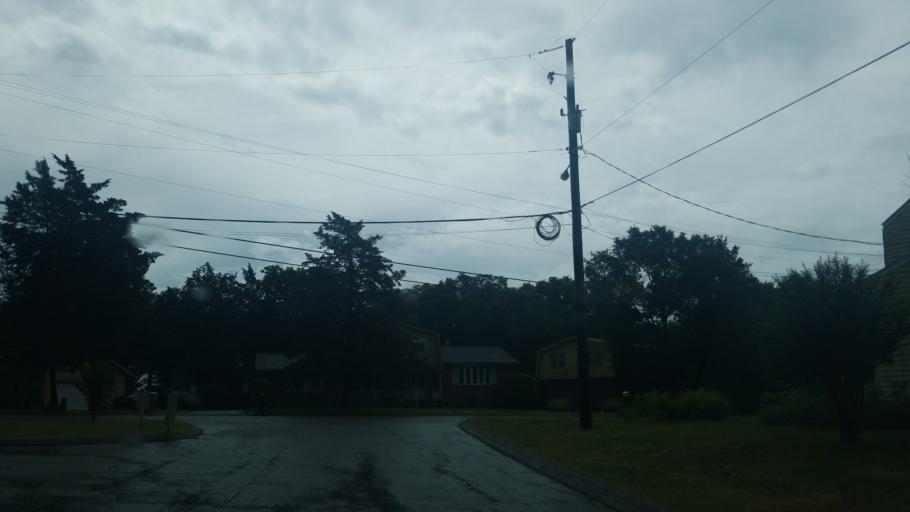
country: US
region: Tennessee
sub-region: Rutherford County
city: La Vergne
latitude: 36.1027
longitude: -86.6059
